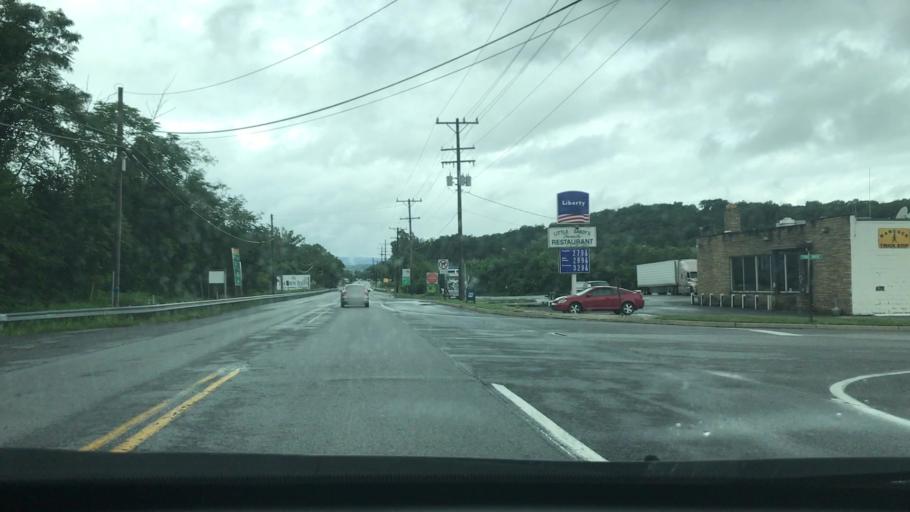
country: US
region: Maryland
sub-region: Washington County
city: Hancock
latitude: 39.6951
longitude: -78.1534
